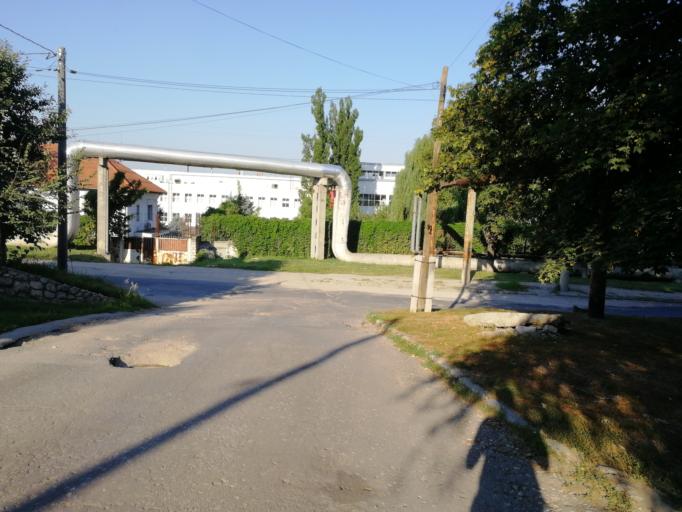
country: MD
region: Chisinau
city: Chisinau
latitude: 47.0248
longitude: 28.8707
